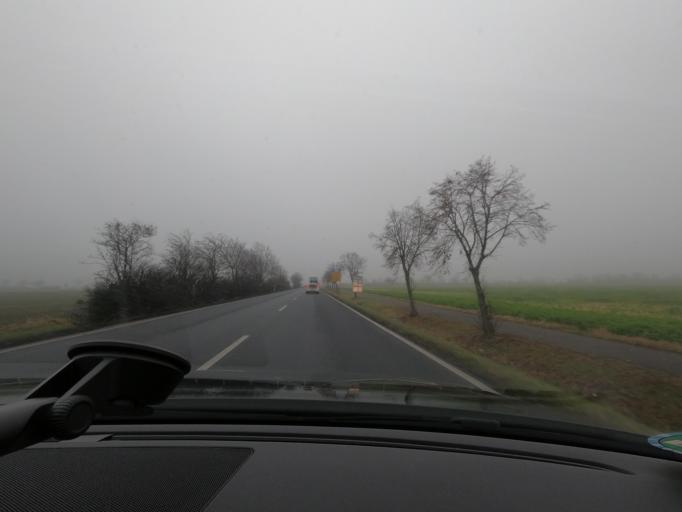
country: DE
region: North Rhine-Westphalia
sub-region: Regierungsbezirk Koln
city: Merzenich
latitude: 50.8255
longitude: 6.5403
